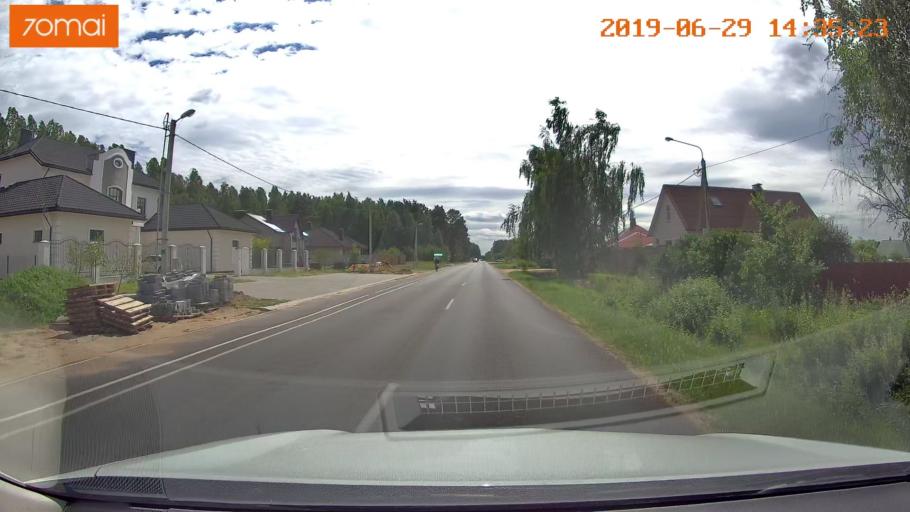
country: BY
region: Minsk
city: Starobin
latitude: 52.7604
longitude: 27.4863
